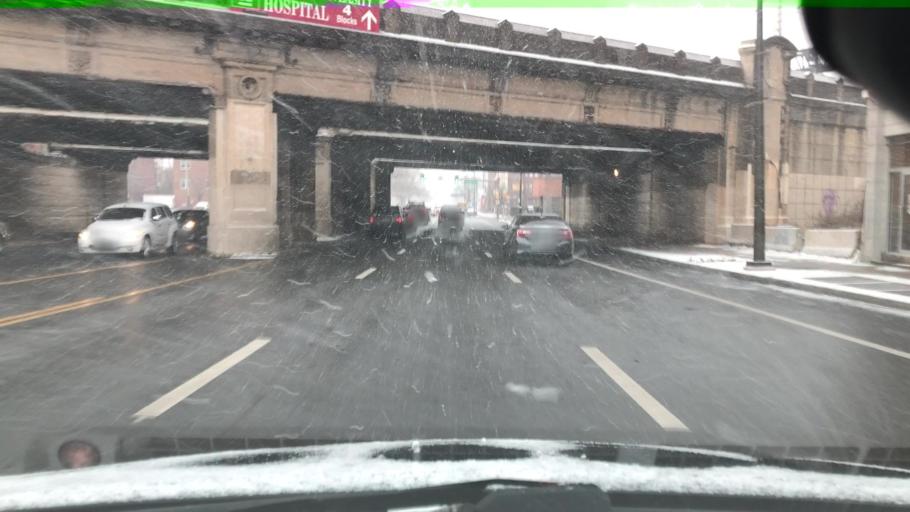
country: US
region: Pennsylvania
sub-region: Philadelphia County
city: Philadelphia
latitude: 39.9973
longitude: -75.1538
